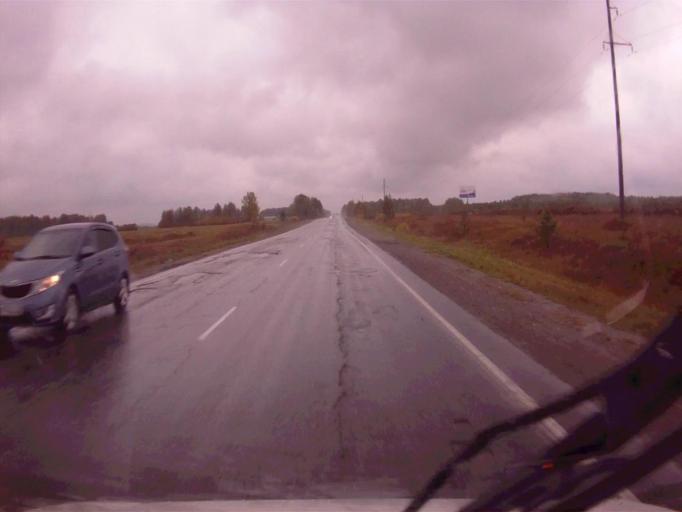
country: RU
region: Chelyabinsk
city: Novogornyy
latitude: 55.4884
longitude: 60.7035
